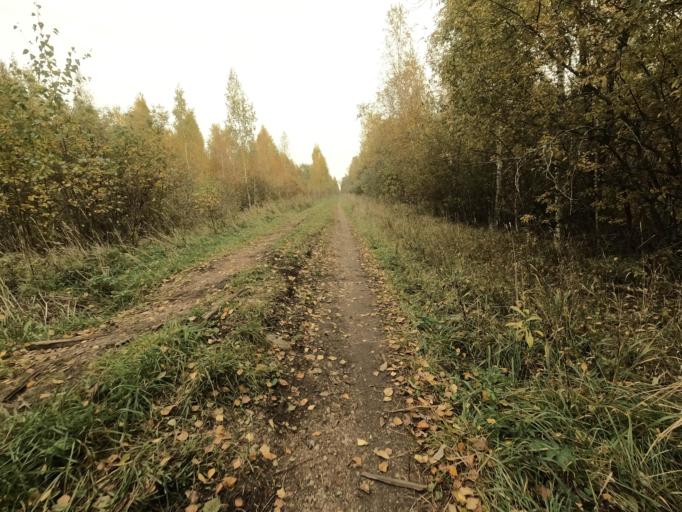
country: RU
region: Novgorod
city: Pankovka
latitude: 58.8842
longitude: 30.9455
